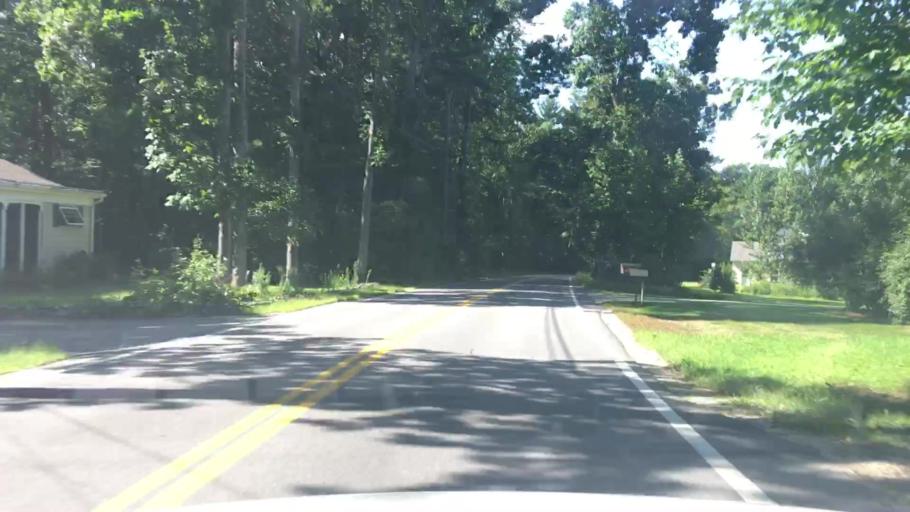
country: US
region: New Hampshire
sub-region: Strafford County
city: Dover
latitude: 43.1823
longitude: -70.8426
